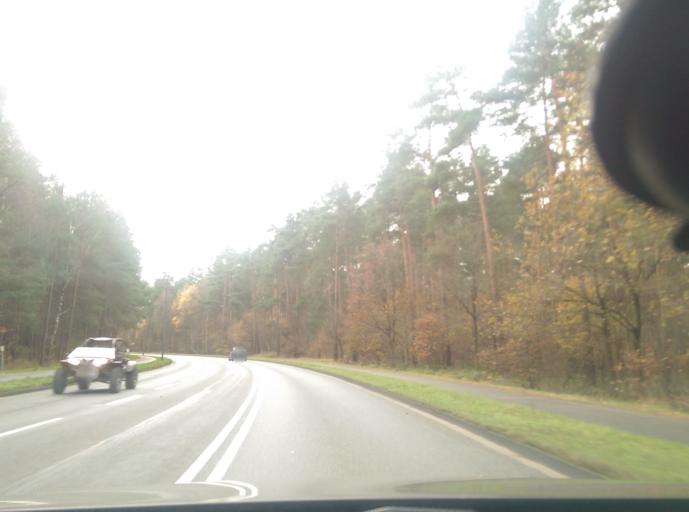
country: DE
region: Lower Saxony
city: Celle
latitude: 52.6145
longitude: 10.0359
